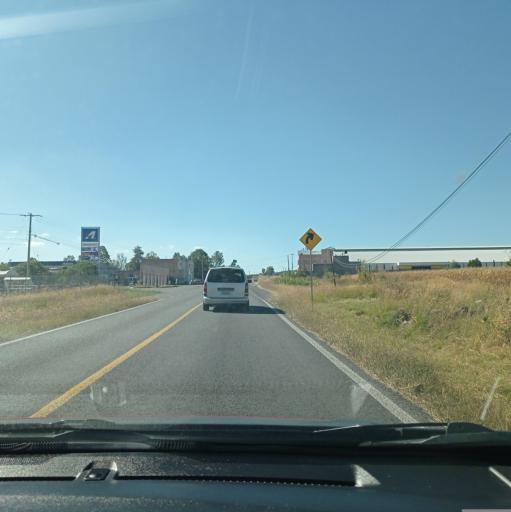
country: MX
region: Jalisco
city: San Miguel el Alto
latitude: 21.0255
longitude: -102.4207
